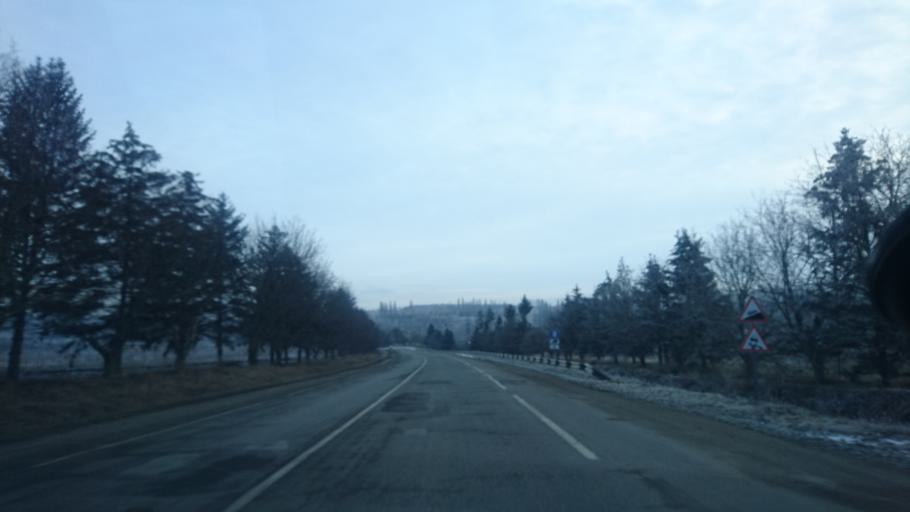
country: MD
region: Briceni
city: Briceni
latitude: 48.2886
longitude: 27.1294
